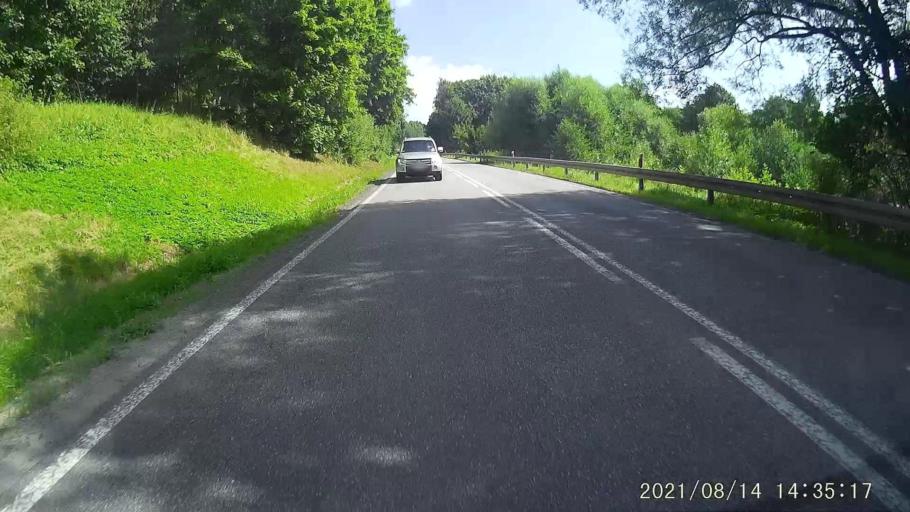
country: PL
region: Lower Silesian Voivodeship
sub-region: Powiat klodzki
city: Nowa Ruda
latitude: 50.5732
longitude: 16.5293
